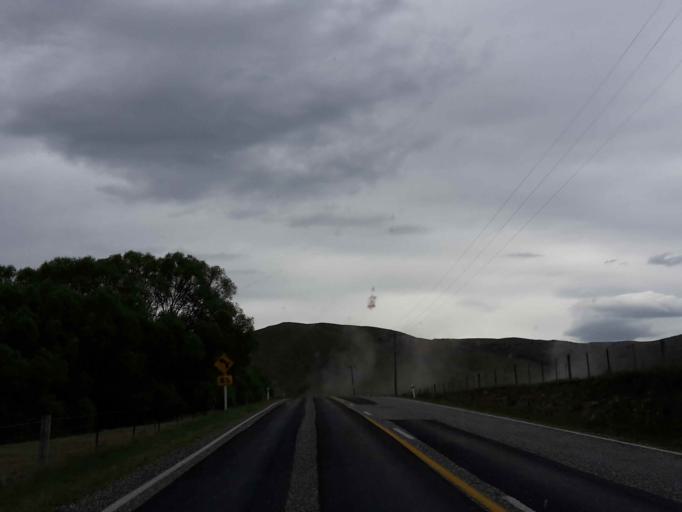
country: NZ
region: Otago
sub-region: Queenstown-Lakes District
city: Wanaka
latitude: -44.7068
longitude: 169.5029
